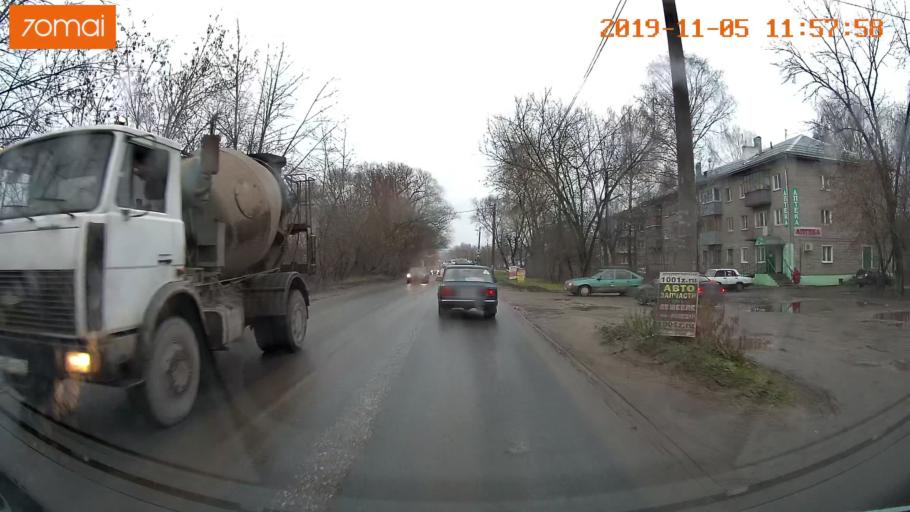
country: RU
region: Ivanovo
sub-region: Gorod Ivanovo
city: Ivanovo
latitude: 56.9818
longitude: 41.0379
